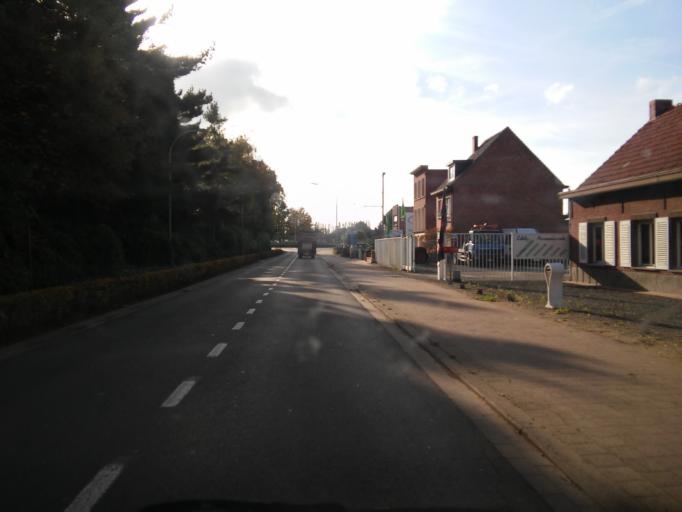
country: BE
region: Flanders
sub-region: Provincie Antwerpen
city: Berlaar
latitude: 51.1005
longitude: 4.6162
